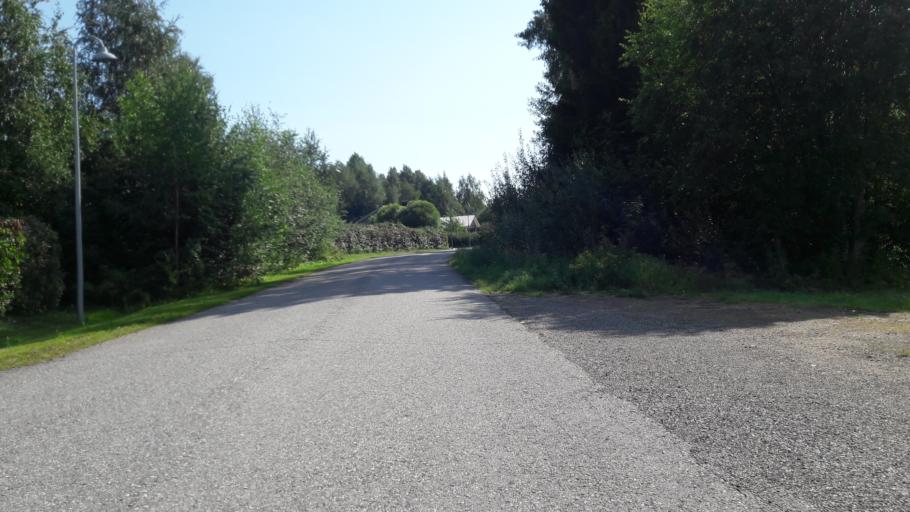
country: FI
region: North Karelia
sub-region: Joensuu
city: Joensuu
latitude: 62.5264
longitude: 29.8384
